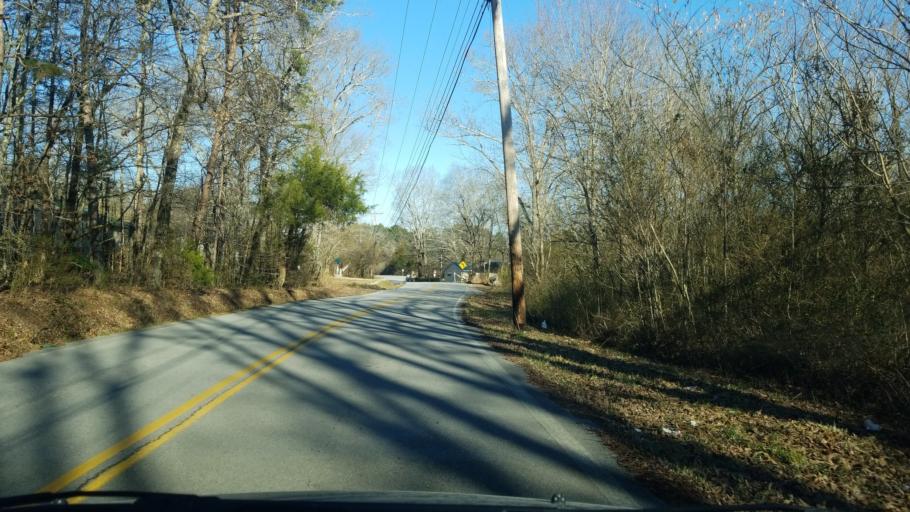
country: US
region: Tennessee
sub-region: Hamilton County
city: Collegedale
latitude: 35.0621
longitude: -85.0966
